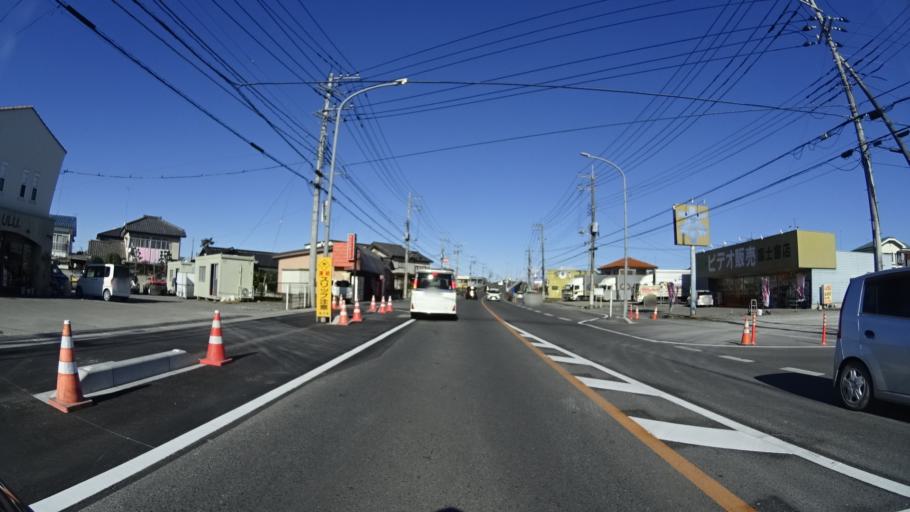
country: JP
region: Tochigi
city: Tochigi
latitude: 36.3979
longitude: 139.7379
